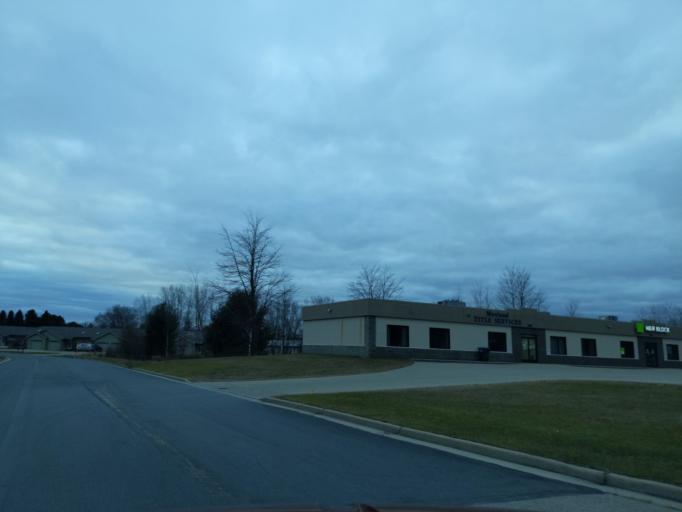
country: US
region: Wisconsin
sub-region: Waushara County
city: Wautoma
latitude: 44.0770
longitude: -89.2982
